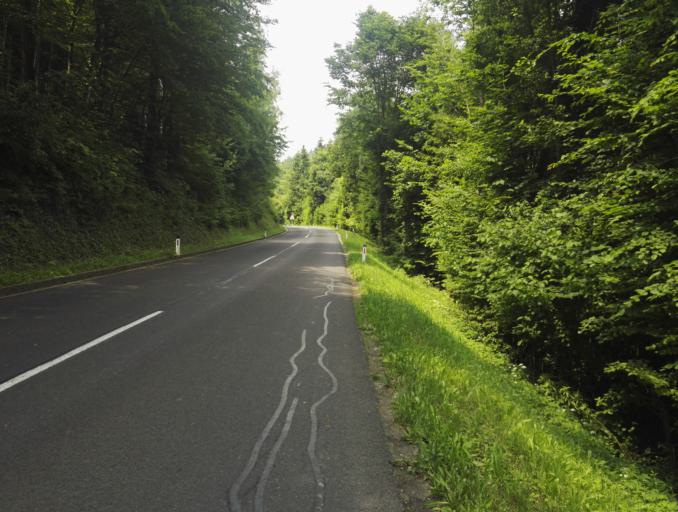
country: AT
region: Styria
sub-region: Politischer Bezirk Graz-Umgebung
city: Gratwein
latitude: 47.0897
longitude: 15.3111
